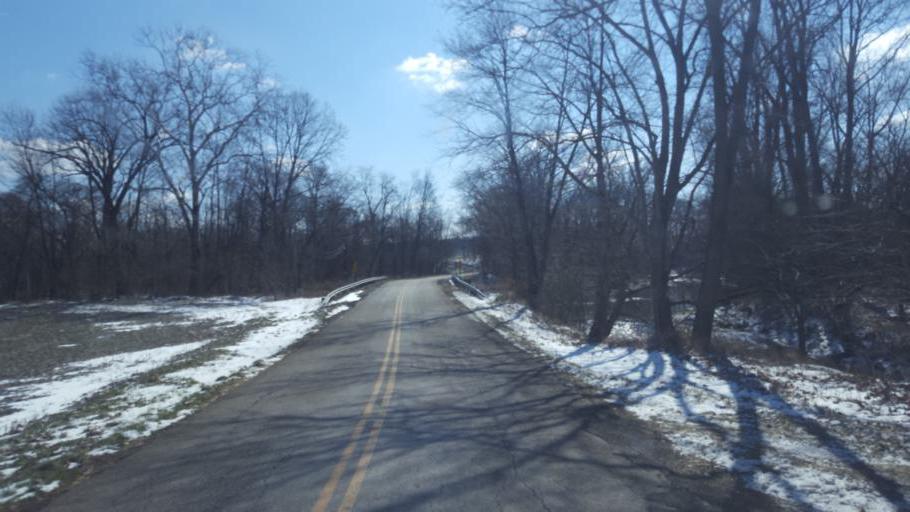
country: US
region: Ohio
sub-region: Licking County
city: Utica
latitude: 40.2622
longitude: -82.4587
